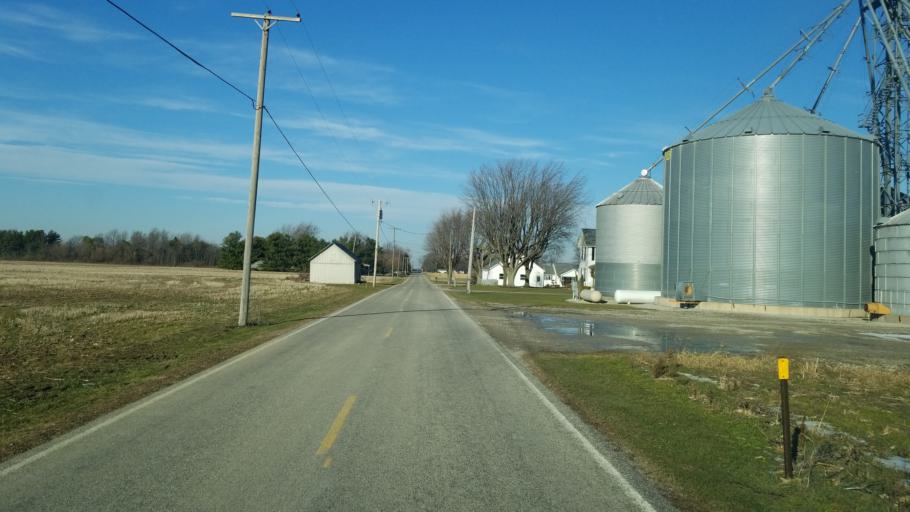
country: US
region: Ohio
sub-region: Sandusky County
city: Mount Carmel
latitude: 41.3071
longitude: -82.9026
